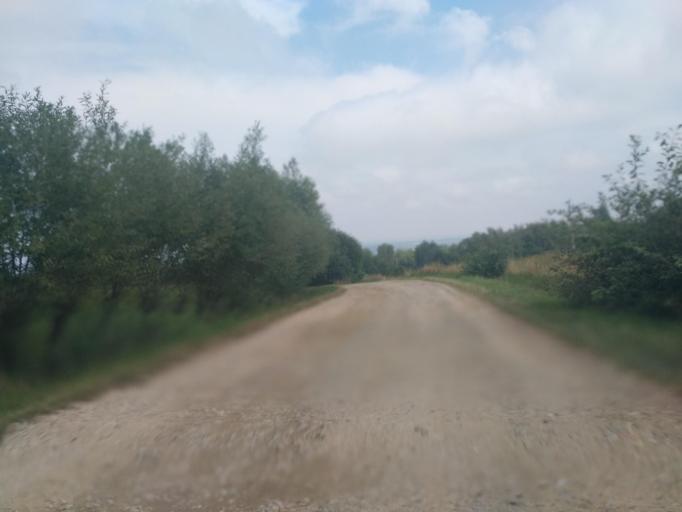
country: PL
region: Subcarpathian Voivodeship
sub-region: Powiat rzeszowski
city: Chmielnik
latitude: 50.0127
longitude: 22.1315
